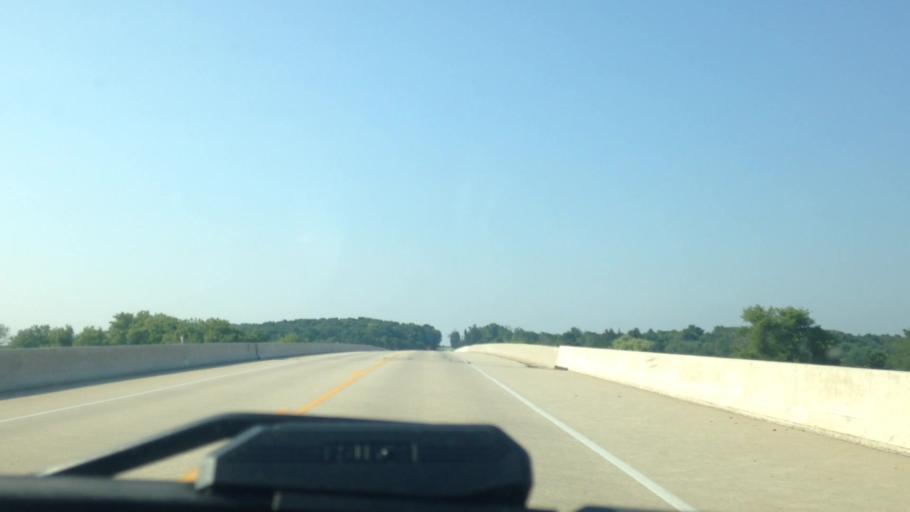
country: US
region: Wisconsin
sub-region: Washington County
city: Slinger
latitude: 43.3118
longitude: -88.2607
